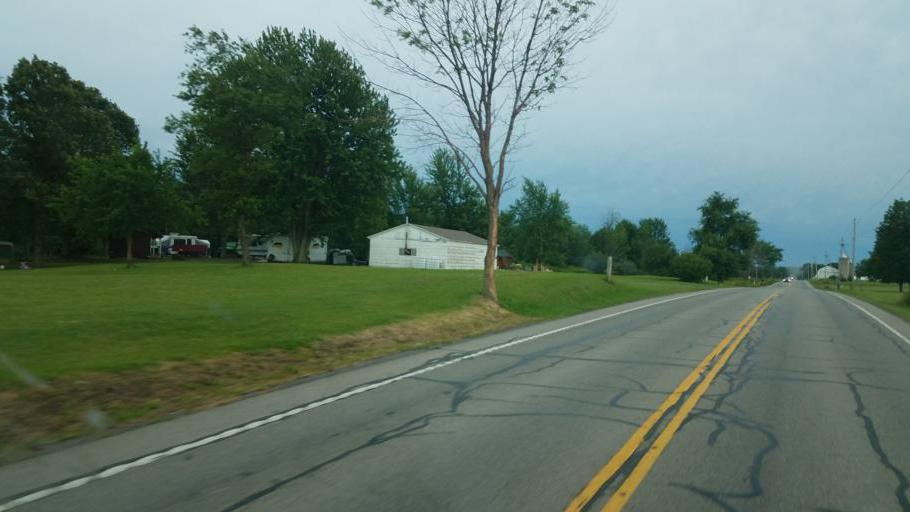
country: US
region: Ohio
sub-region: Huron County
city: Greenwich
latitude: 40.9282
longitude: -82.4968
